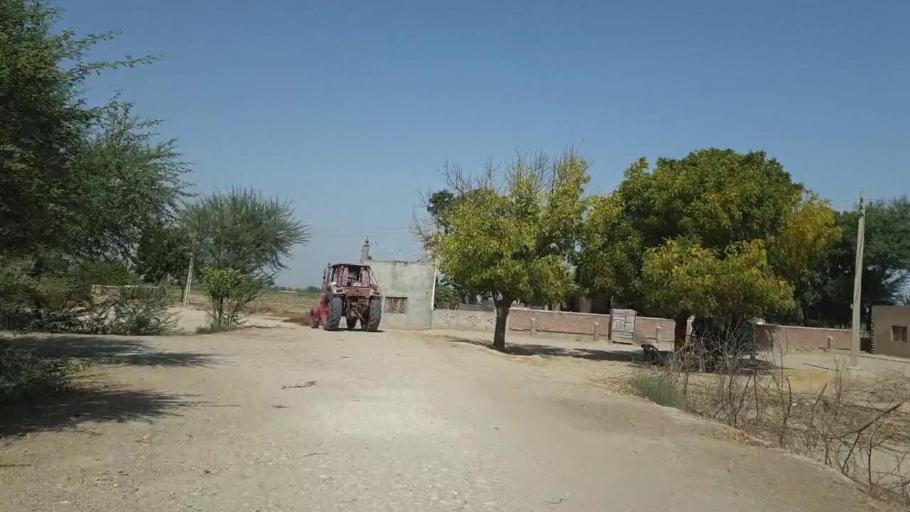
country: PK
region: Sindh
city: Naukot
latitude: 24.9590
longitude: 69.4909
